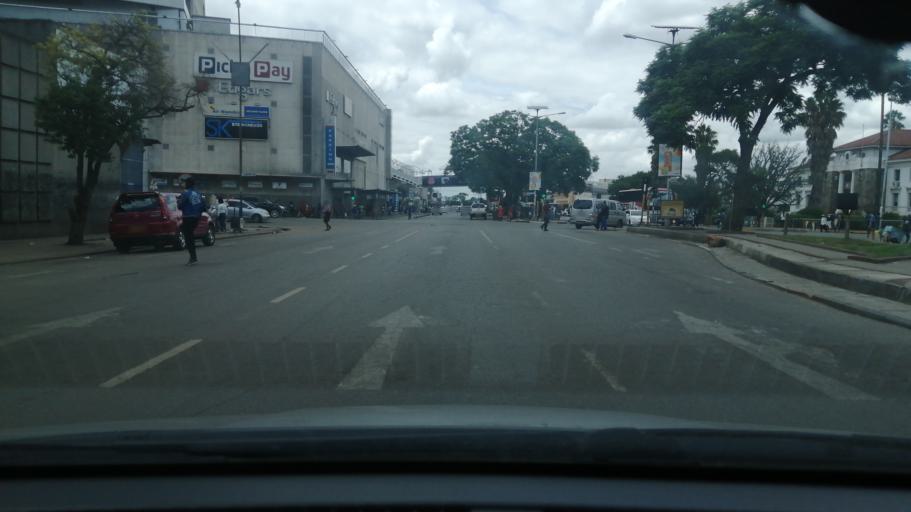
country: ZW
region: Harare
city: Harare
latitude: -17.8309
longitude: 31.0469
